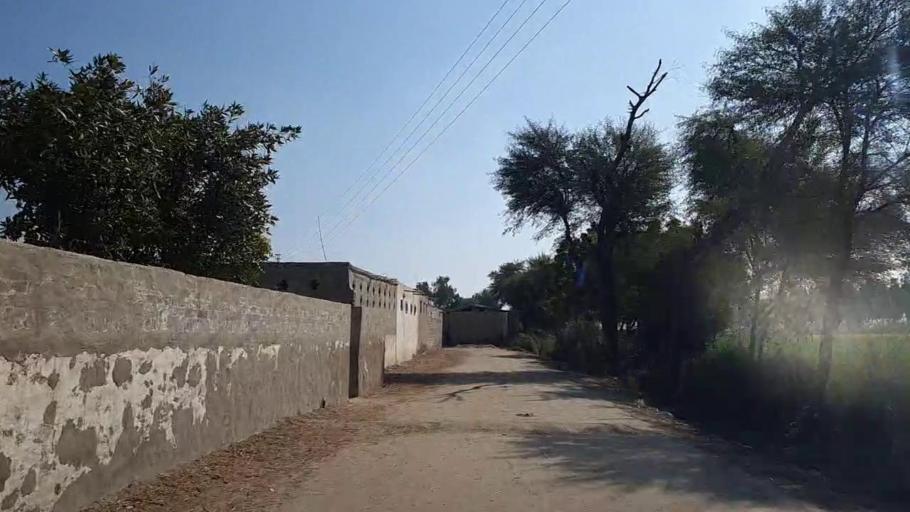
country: PK
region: Sindh
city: Nawabshah
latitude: 26.3484
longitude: 68.3799
